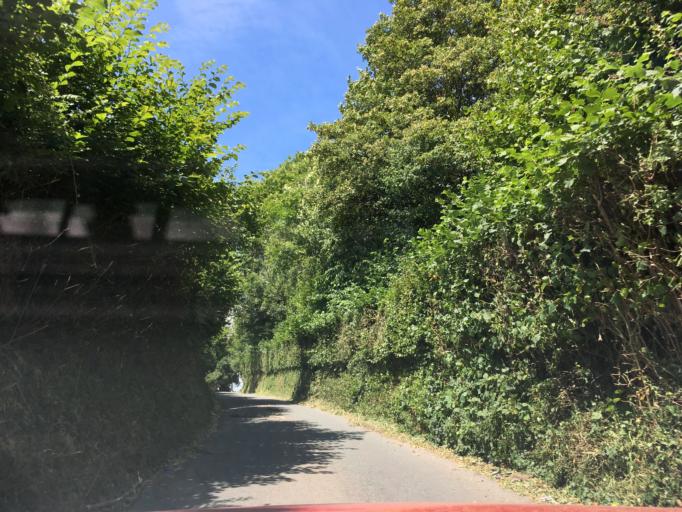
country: GB
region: Wales
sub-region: Caerphilly County Borough
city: Machen
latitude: 51.5515
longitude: -3.1429
